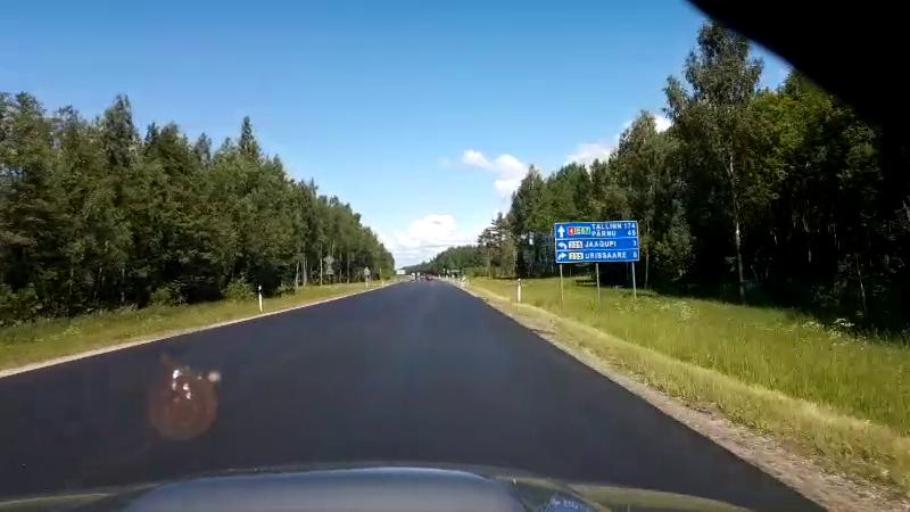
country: LV
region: Salacgrivas
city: Ainazi
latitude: 58.0321
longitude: 24.5052
